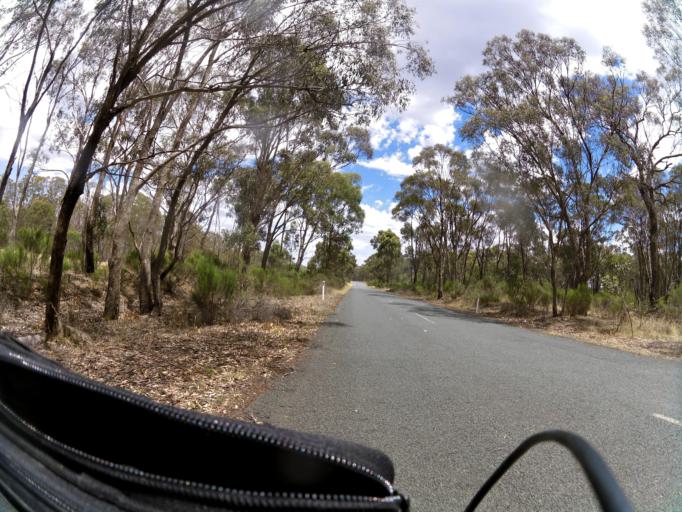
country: AU
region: Victoria
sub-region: Greater Shepparton
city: Shepparton
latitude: -36.6839
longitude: 145.1864
